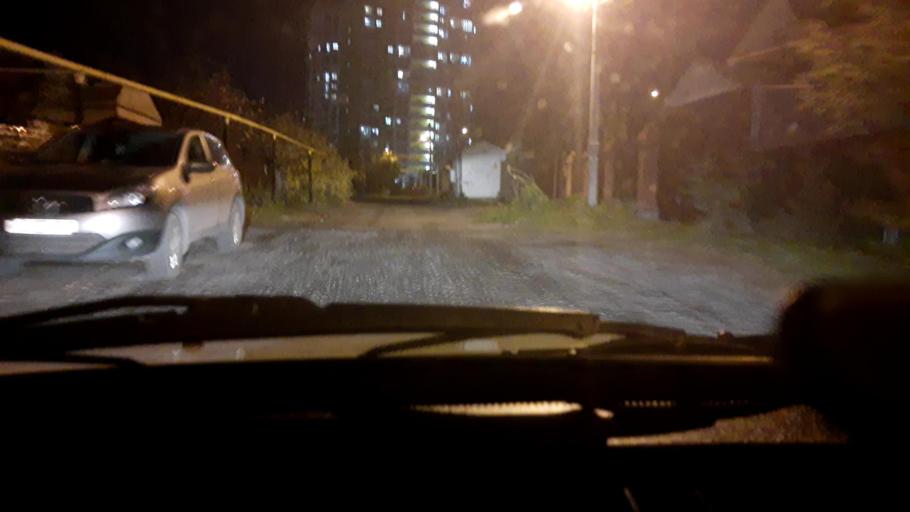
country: RU
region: Bashkortostan
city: Ufa
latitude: 54.7102
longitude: 55.9831
